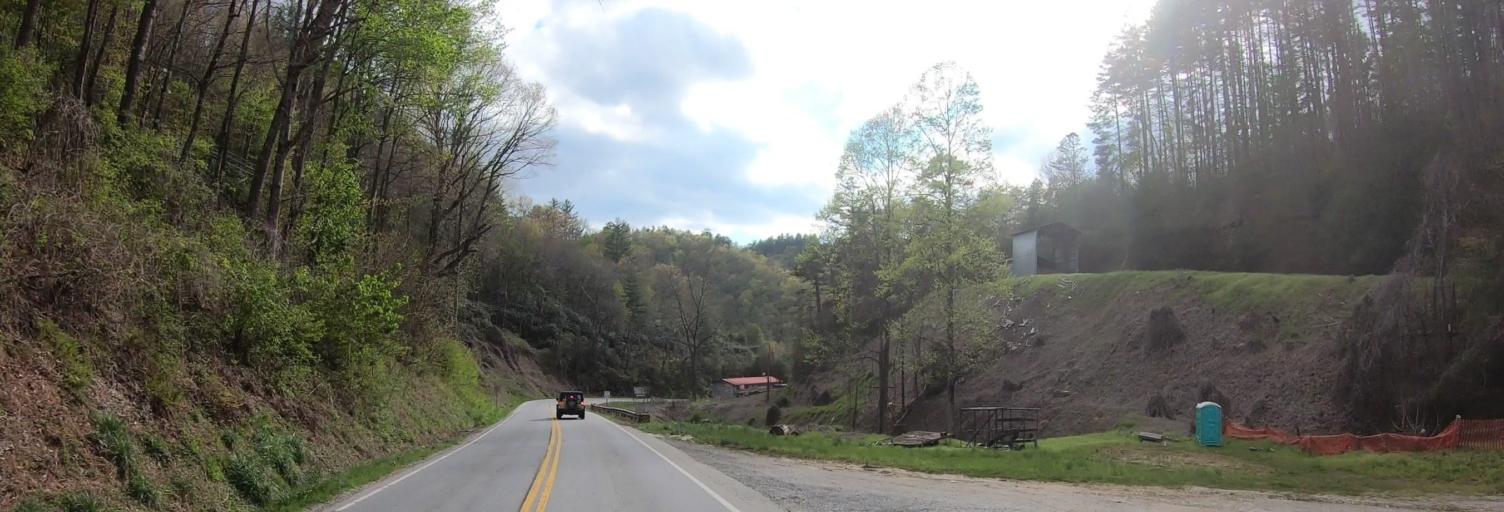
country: US
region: North Carolina
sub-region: Swain County
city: Bryson City
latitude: 35.3297
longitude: -83.5783
